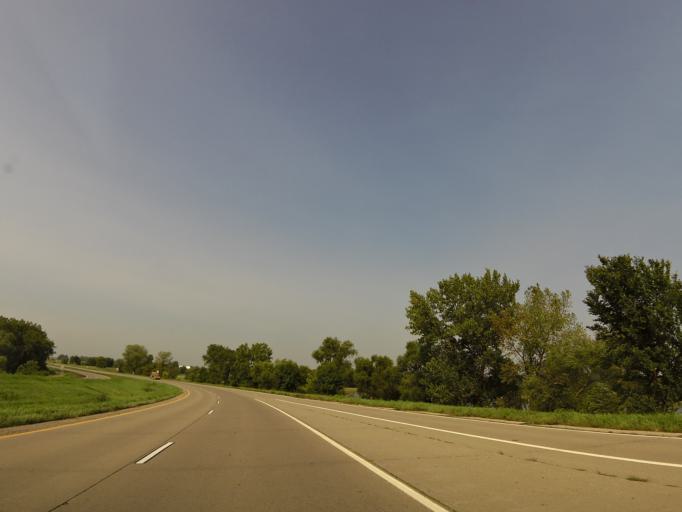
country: US
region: Minnesota
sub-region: Carver County
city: Cologne
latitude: 44.7692
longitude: -93.7937
